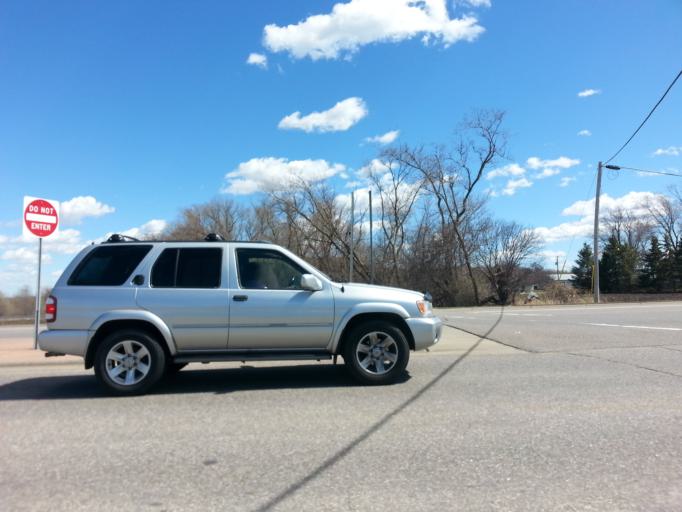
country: US
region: Minnesota
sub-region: Dakota County
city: Lakeville
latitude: 44.6815
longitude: -93.2513
